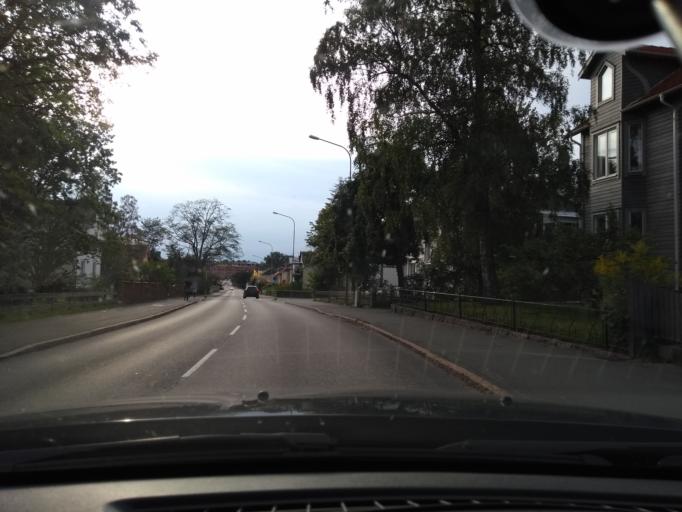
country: SE
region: Joenkoeping
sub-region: Nassjo Kommun
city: Nassjo
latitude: 57.6503
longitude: 14.7105
